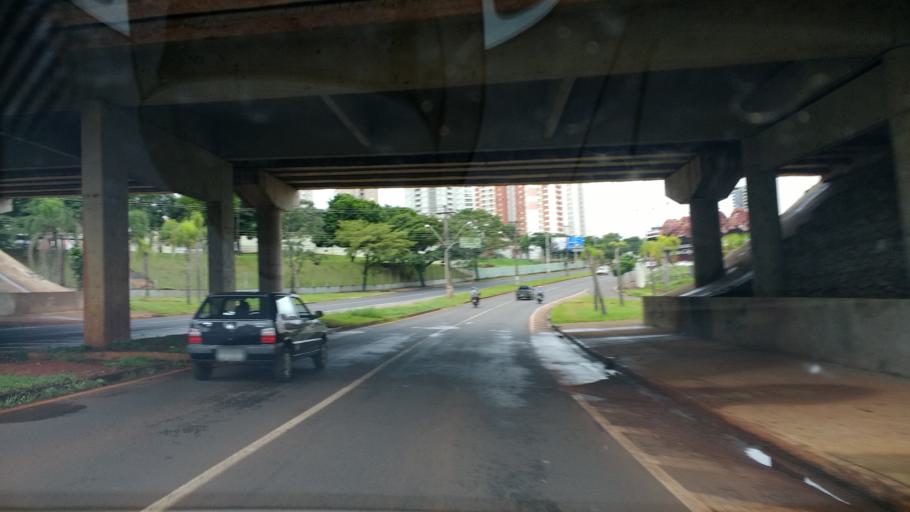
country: BR
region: Parana
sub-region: Londrina
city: Londrina
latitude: -23.3372
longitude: -51.1840
